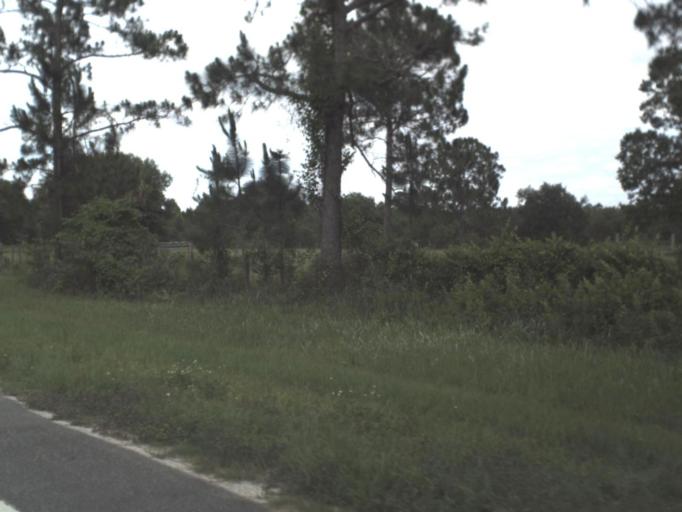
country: US
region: Florida
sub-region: Clay County
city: Keystone Heights
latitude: 29.8718
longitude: -81.9331
